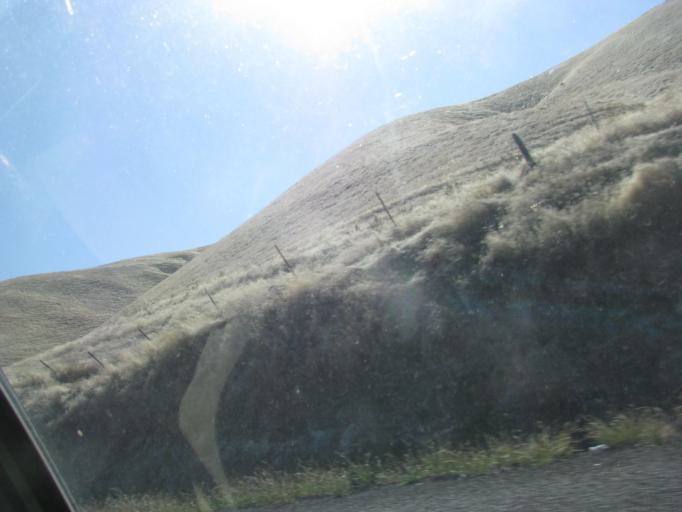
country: US
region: Washington
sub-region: Asotin County
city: Asotin
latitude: 46.3199
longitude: -117.0529
